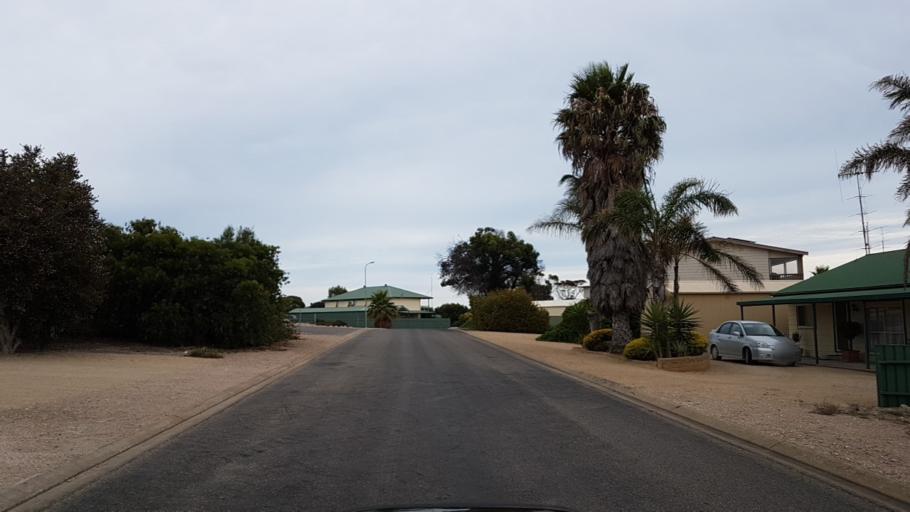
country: AU
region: South Australia
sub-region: Yorke Peninsula
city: Port Victoria
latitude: -34.9090
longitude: 137.0513
